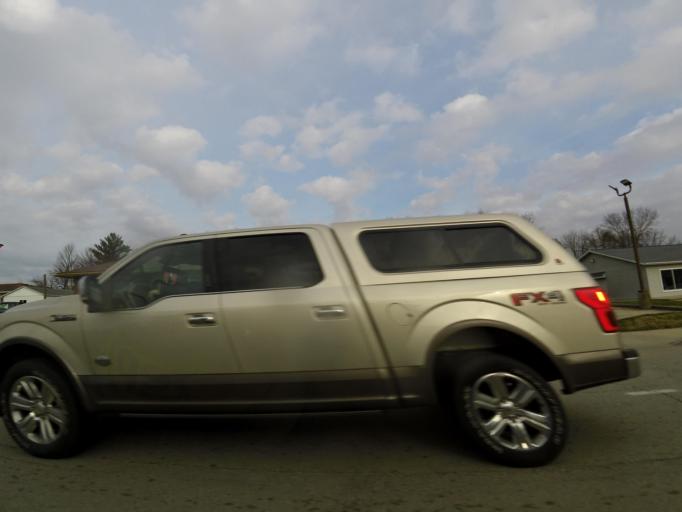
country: US
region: Illinois
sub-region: Christian County
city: Pana
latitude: 39.3902
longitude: -89.0713
